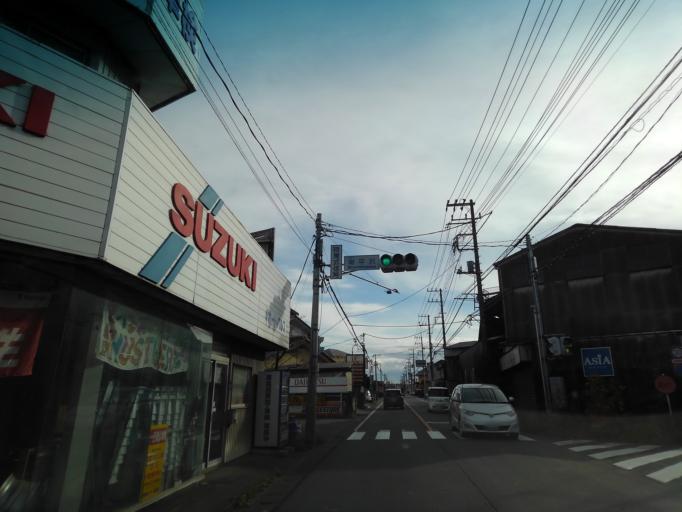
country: JP
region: Saitama
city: Morohongo
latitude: 35.9106
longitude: 139.3327
